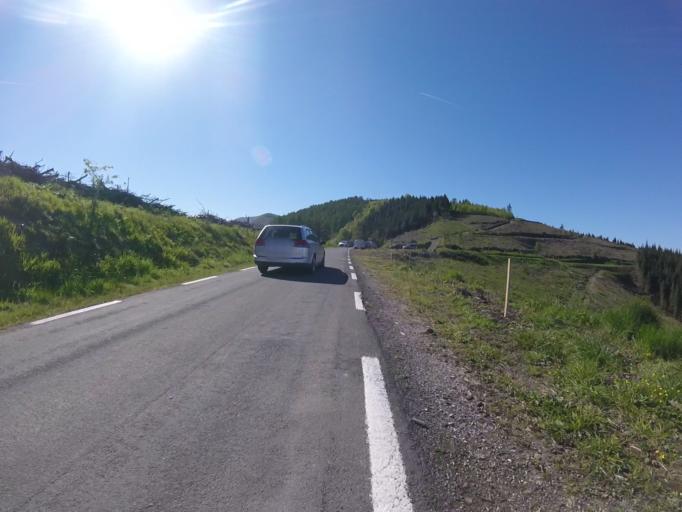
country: ES
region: Basque Country
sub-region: Provincia de Guipuzcoa
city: Errezil
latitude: 43.2034
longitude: -2.1979
